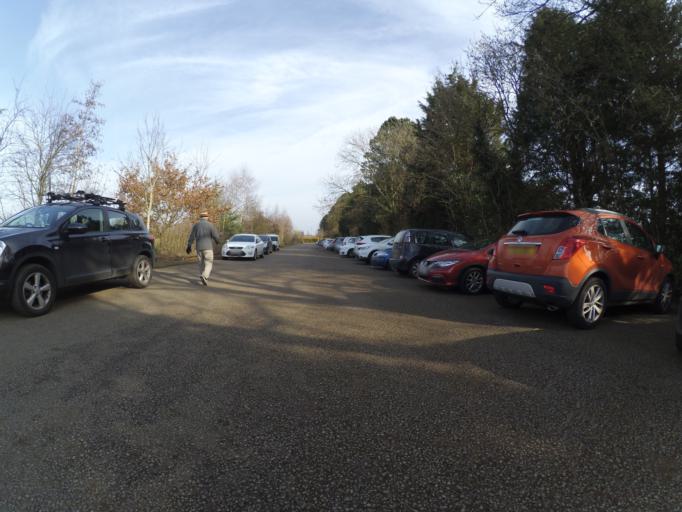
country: GB
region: England
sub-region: Warwickshire
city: Rugby
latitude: 52.3714
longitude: -1.2377
